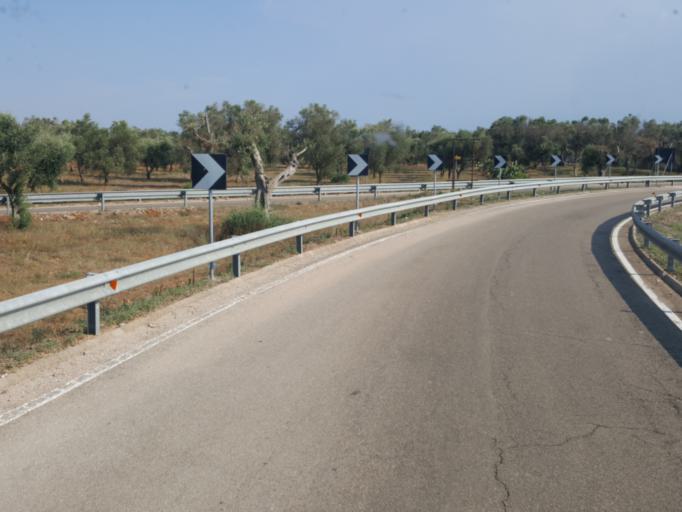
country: IT
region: Apulia
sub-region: Provincia di Lecce
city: Trepuzzi
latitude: 40.4400
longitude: 18.0804
